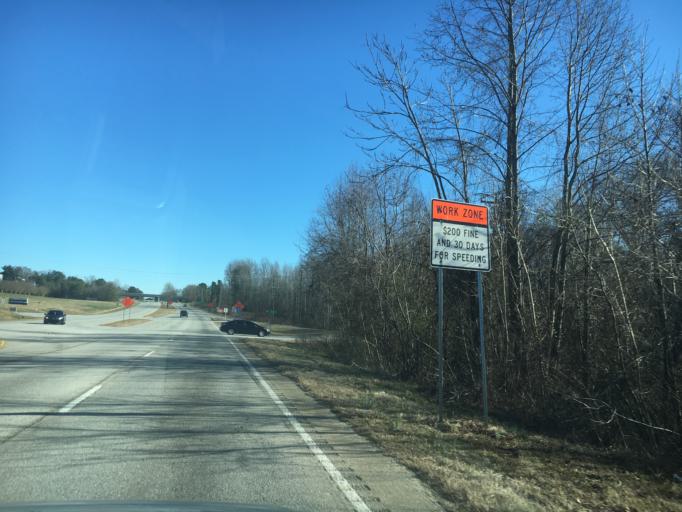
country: US
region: South Carolina
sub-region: Spartanburg County
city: Wellford
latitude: 34.9412
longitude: -82.0821
